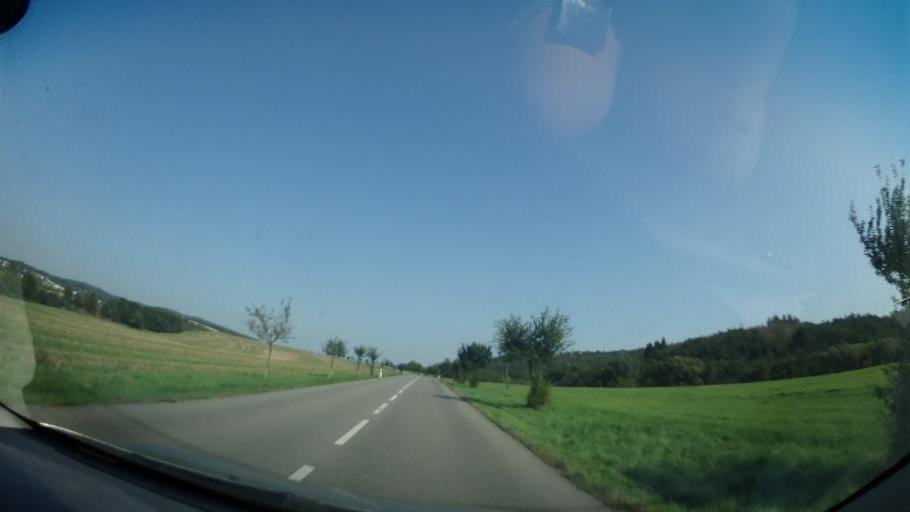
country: CZ
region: South Moravian
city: Kurim
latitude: 49.2431
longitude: 16.5301
